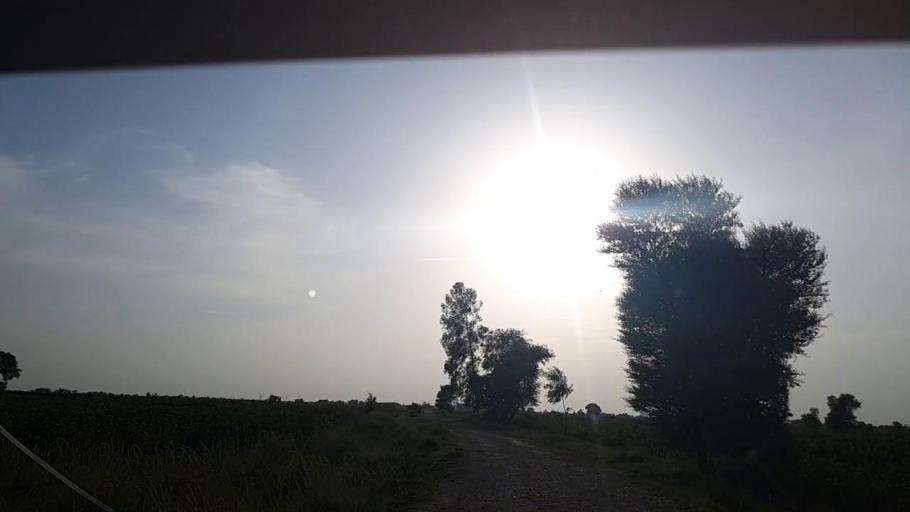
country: PK
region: Sindh
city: Khanpur
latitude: 27.8092
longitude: 69.3250
